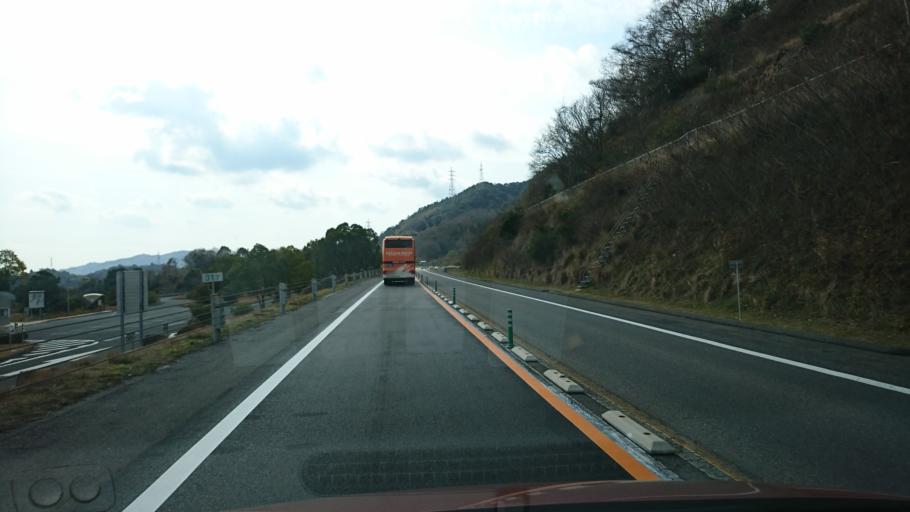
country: JP
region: Hiroshima
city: Innoshima
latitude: 34.2308
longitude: 133.0475
